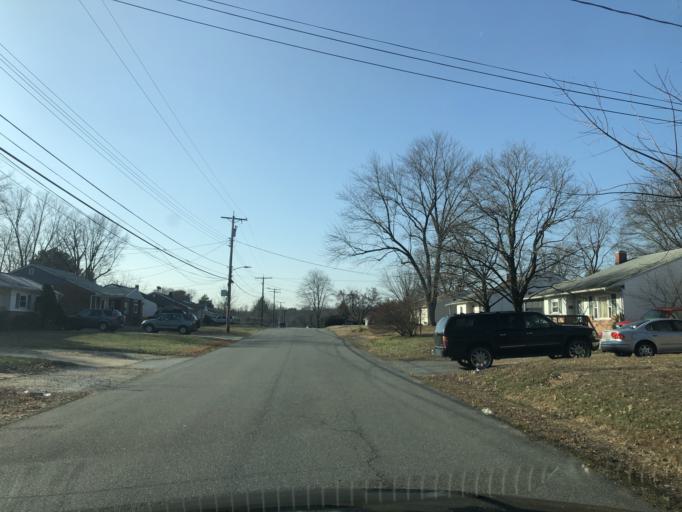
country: US
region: Maryland
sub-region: Anne Arundel County
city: Odenton
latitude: 39.0783
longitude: -76.6996
